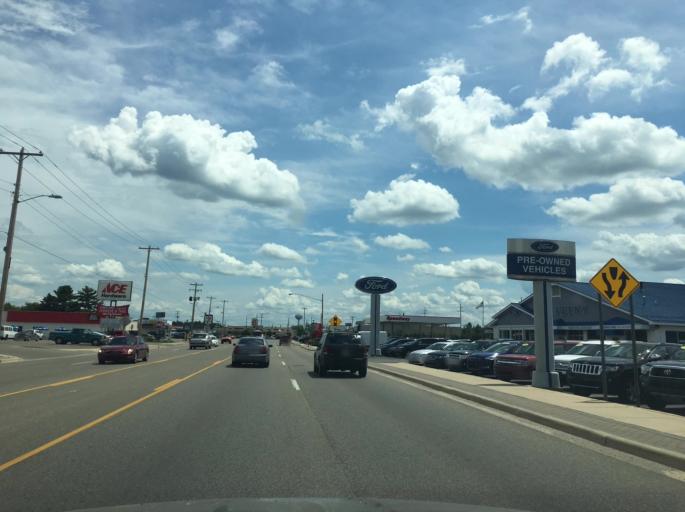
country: US
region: Michigan
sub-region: Crawford County
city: Grayling
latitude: 44.6583
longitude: -84.7107
